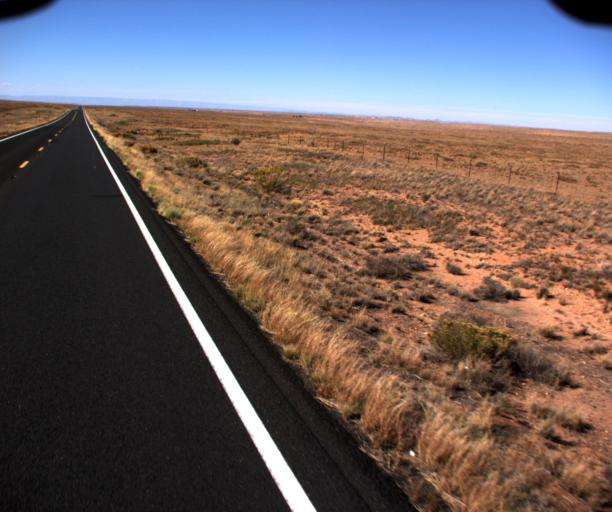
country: US
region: Arizona
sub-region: Coconino County
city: Tuba City
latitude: 36.0147
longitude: -111.0901
